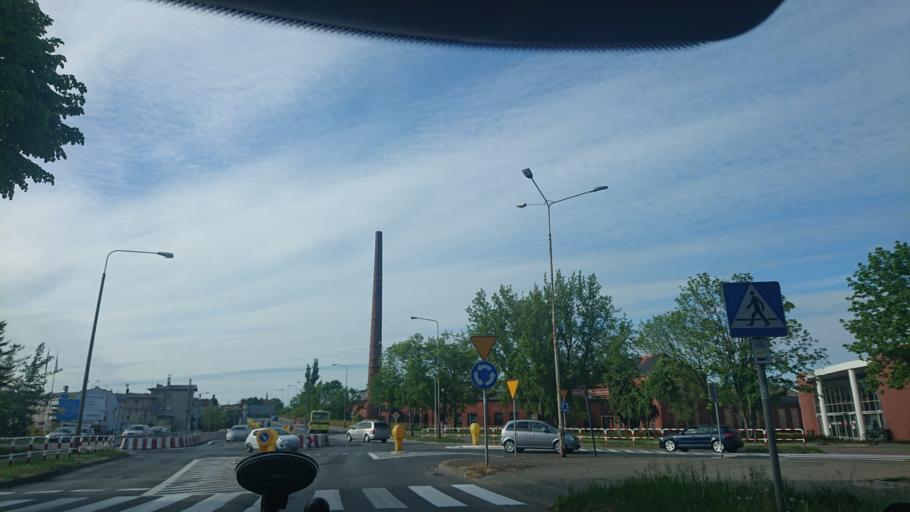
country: PL
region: Greater Poland Voivodeship
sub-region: Powiat gnieznienski
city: Gniezno
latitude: 52.5265
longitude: 17.5975
